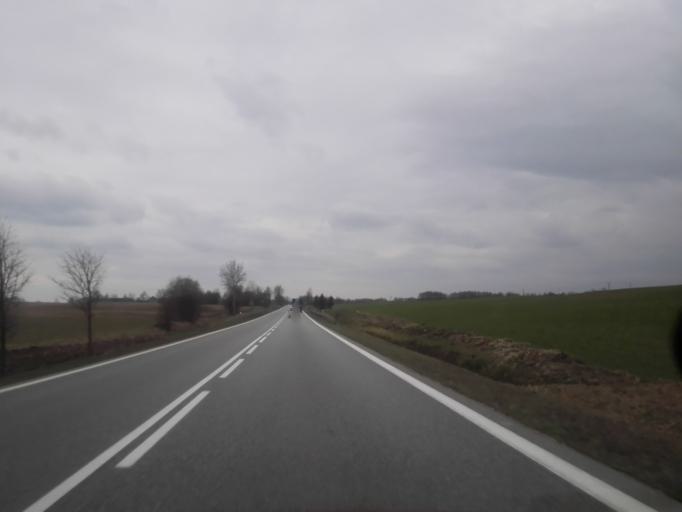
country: PL
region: Podlasie
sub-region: Powiat augustowski
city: Augustow
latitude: 53.8112
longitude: 22.9119
